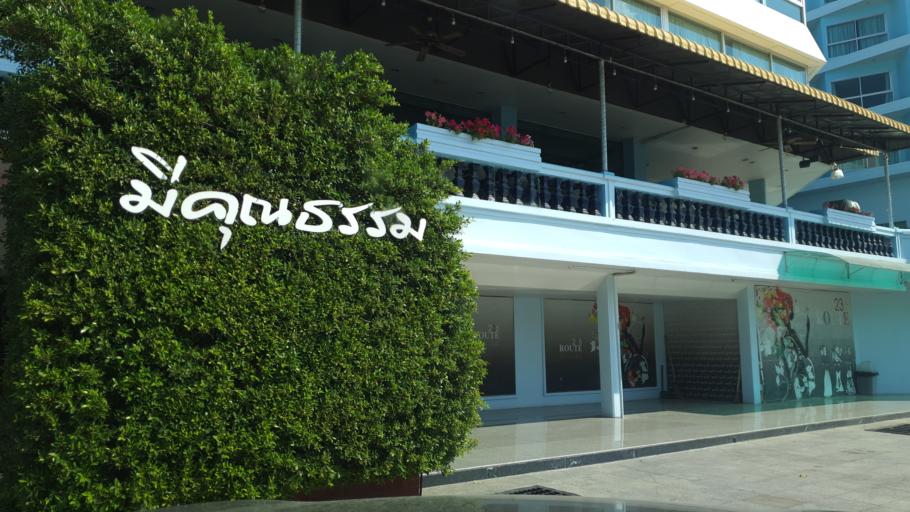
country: TH
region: Tak
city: Tak
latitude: 16.8722
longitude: 99.1229
